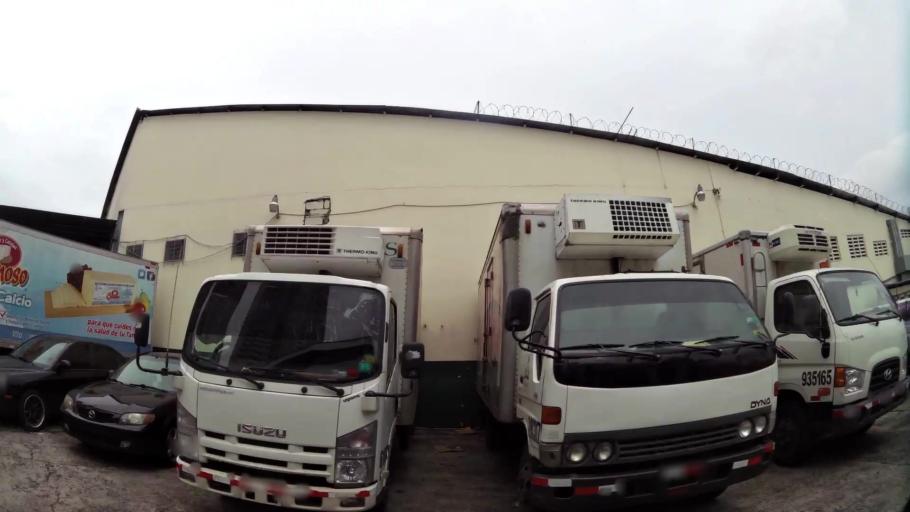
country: PA
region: Panama
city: Panama
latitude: 8.9955
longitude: -79.5296
